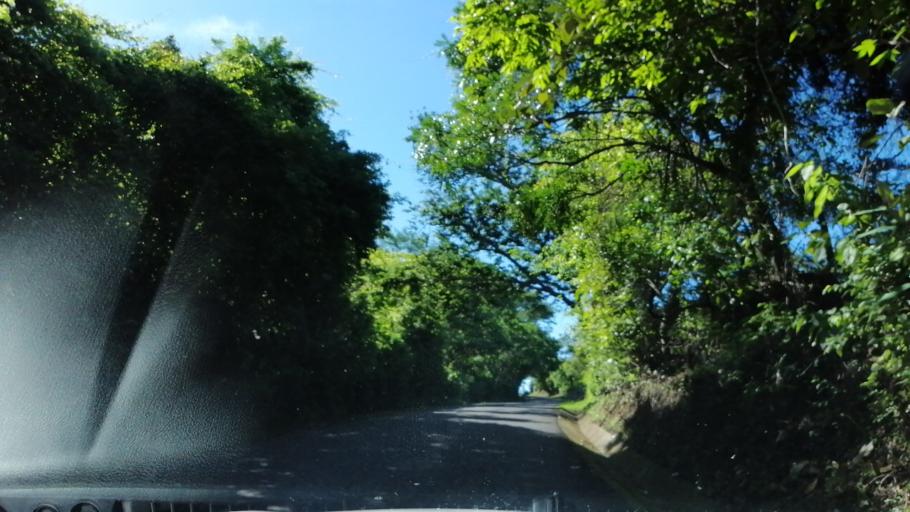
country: SV
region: Morazan
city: Corinto
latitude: 13.8110
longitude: -87.9954
